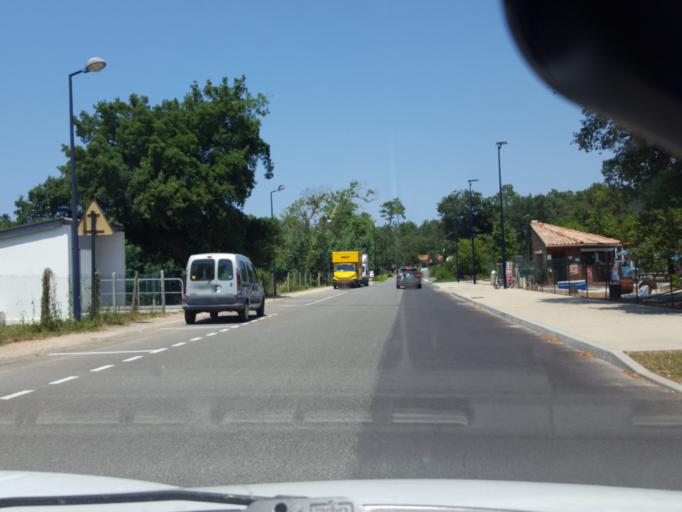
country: FR
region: Aquitaine
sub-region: Departement des Landes
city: Ondres
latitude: 43.5724
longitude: -1.4712
